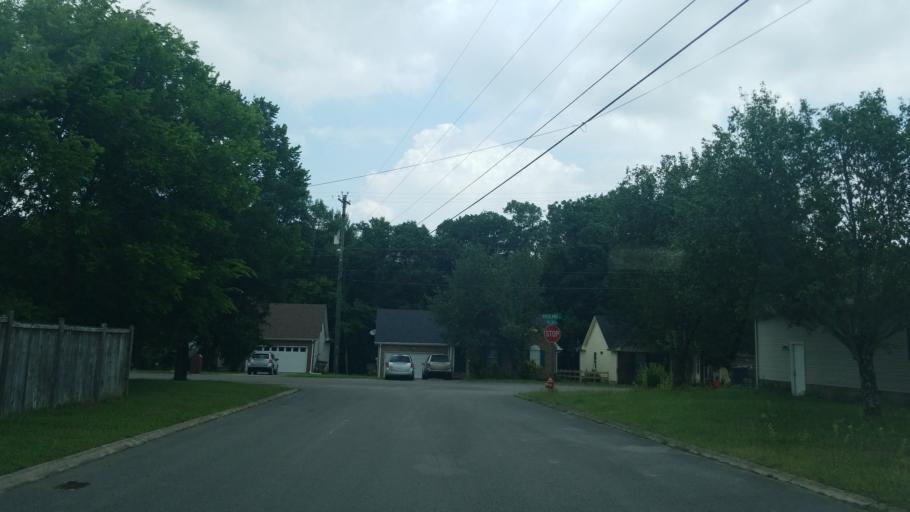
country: US
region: Tennessee
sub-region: Rutherford County
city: La Vergne
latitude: 36.0333
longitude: -86.5886
